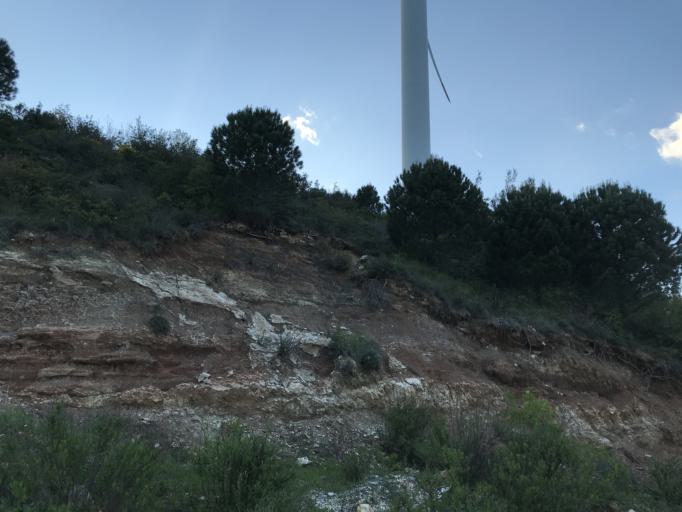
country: TR
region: Hatay
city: Buyukcat
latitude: 36.1050
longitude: 36.0440
